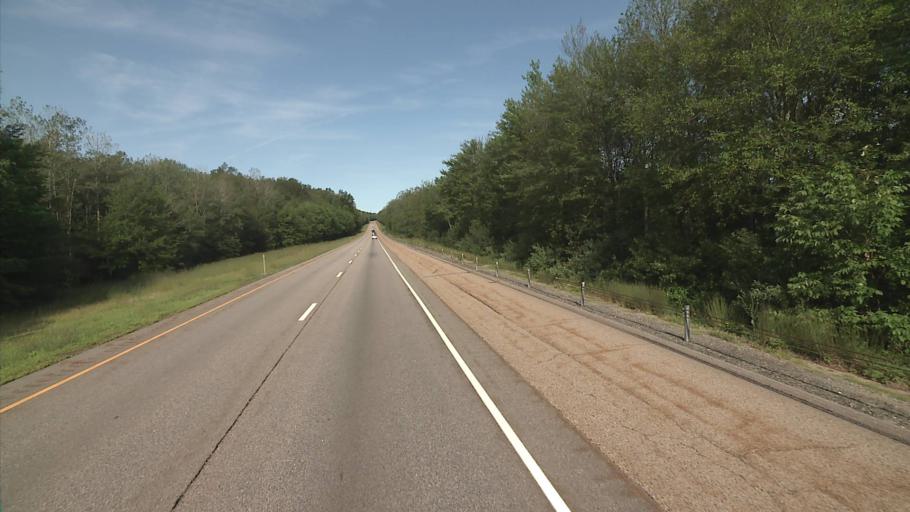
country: US
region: Connecticut
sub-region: New London County
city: Colchester
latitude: 41.5687
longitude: -72.2670
